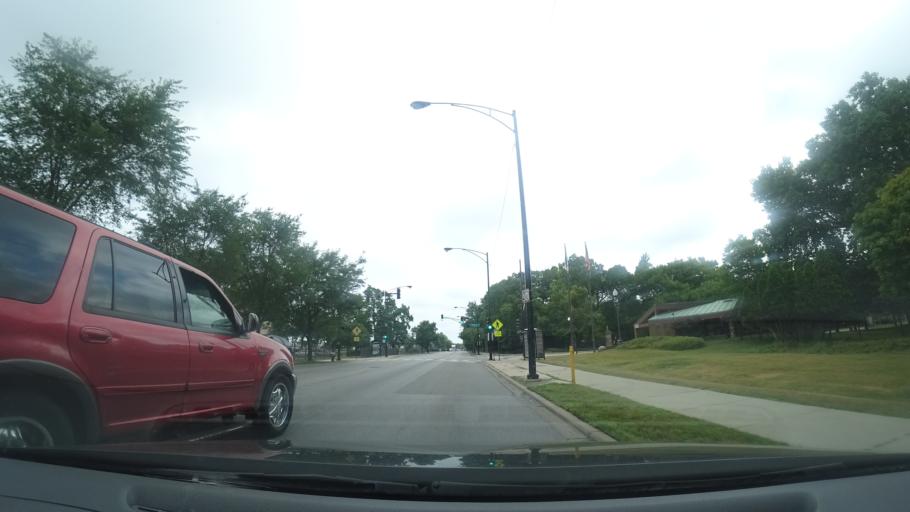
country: US
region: Illinois
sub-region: Cook County
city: Lincolnwood
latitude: 41.9855
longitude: -87.7285
